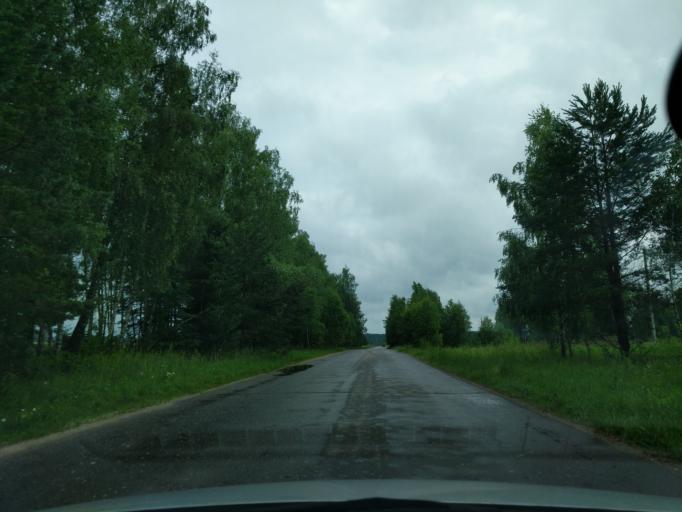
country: RU
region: Kaluga
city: Myatlevo
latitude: 54.8198
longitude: 35.6743
